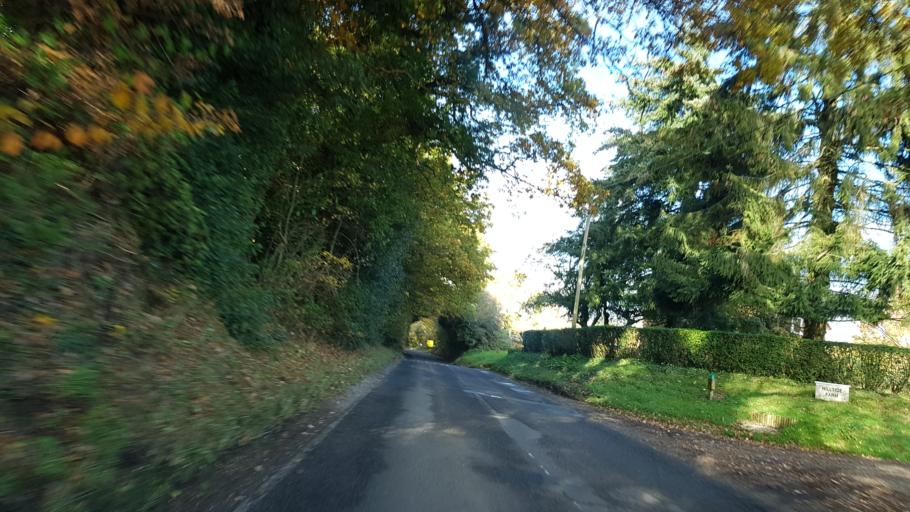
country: GB
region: England
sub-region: Surrey
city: Churt
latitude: 51.1406
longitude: -0.7532
